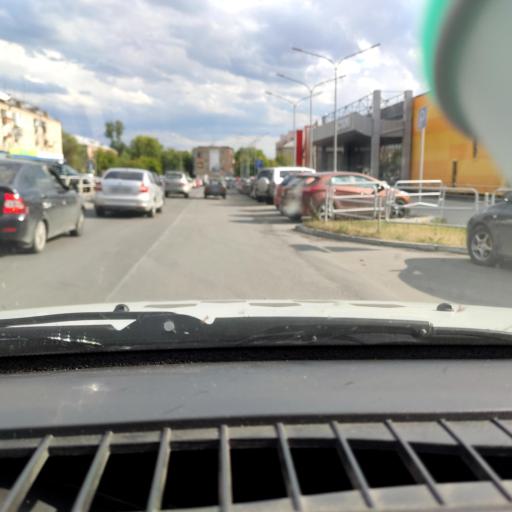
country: RU
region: Chelyabinsk
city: Miass
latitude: 55.0470
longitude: 60.1115
